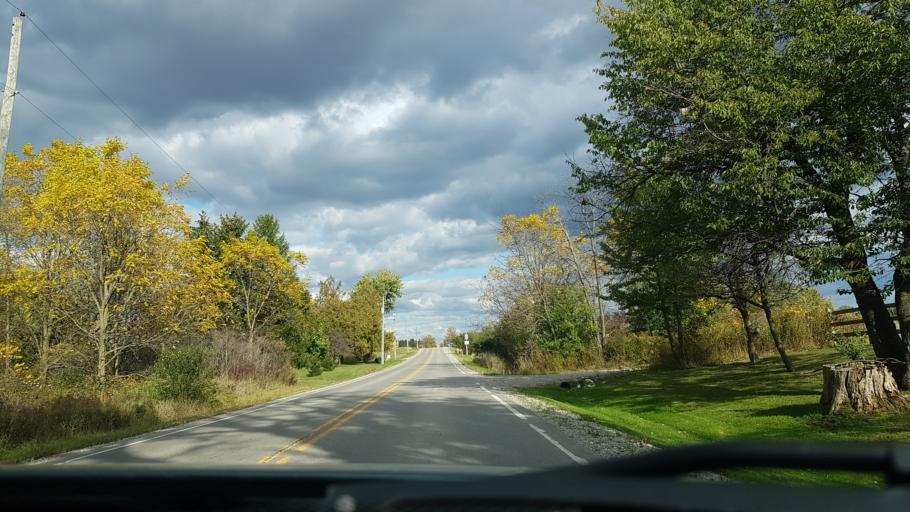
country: CA
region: Ontario
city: Delaware
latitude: 43.0152
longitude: -81.3677
